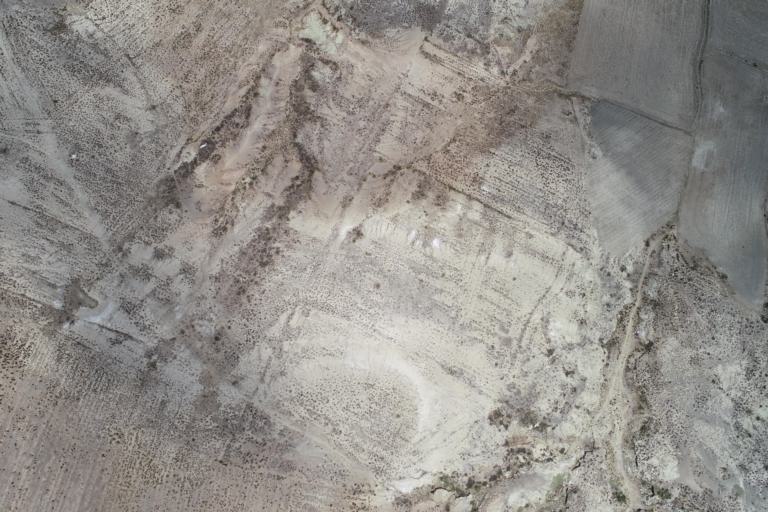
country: BO
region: La Paz
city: Achacachi
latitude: -16.0441
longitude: -68.6952
